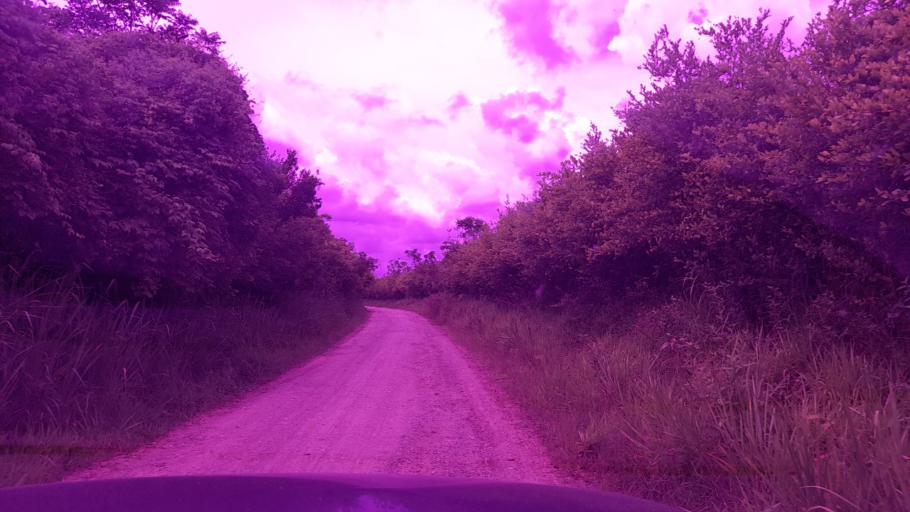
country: CO
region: Valle del Cauca
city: Andalucia
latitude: 4.1693
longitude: -76.0816
